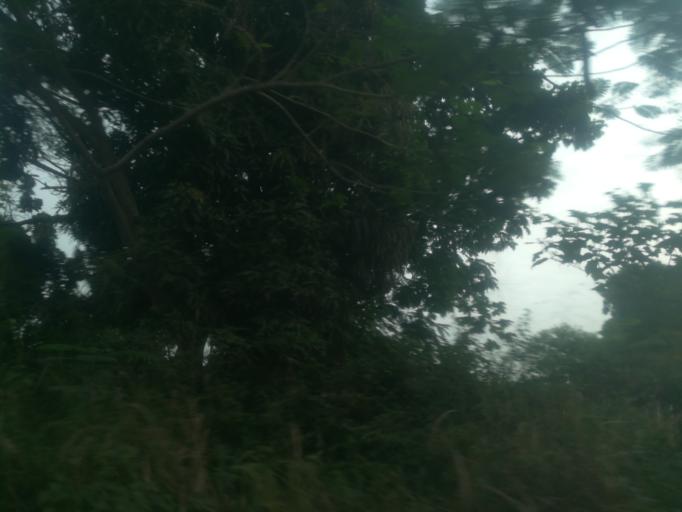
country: NG
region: Ogun
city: Abeokuta
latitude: 7.1993
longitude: 3.2221
